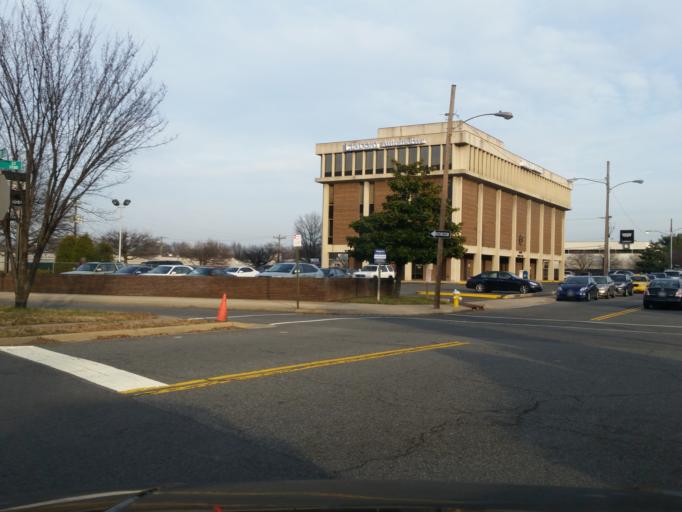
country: US
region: Virginia
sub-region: Fairfax County
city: Huntington
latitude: 38.8282
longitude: -77.0863
